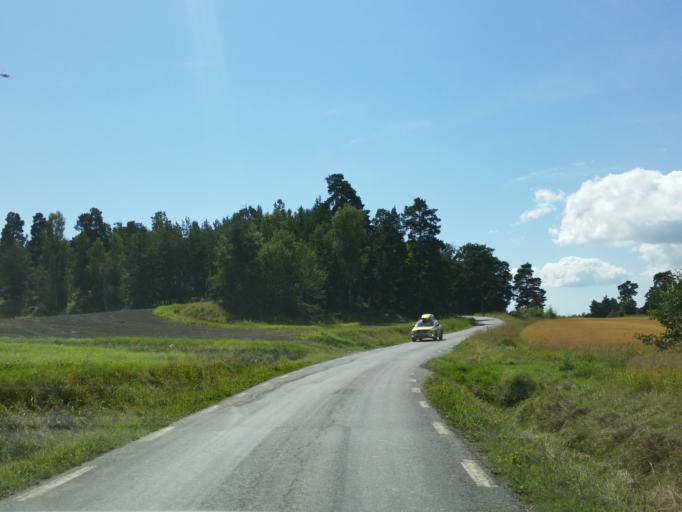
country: SE
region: Soedermanland
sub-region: Trosa Kommun
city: Trosa
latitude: 58.9735
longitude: 17.6515
